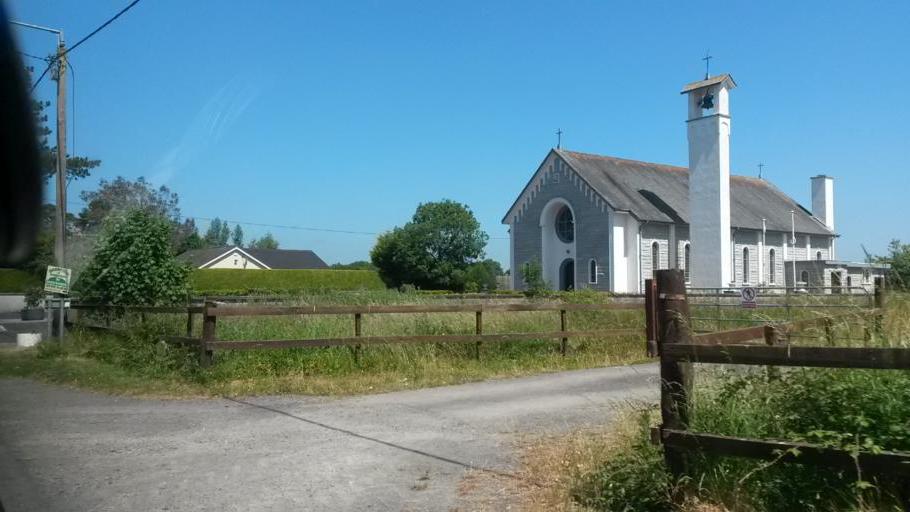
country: IE
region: Leinster
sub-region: An Mhi
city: Ashbourne
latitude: 53.5226
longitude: -6.3154
